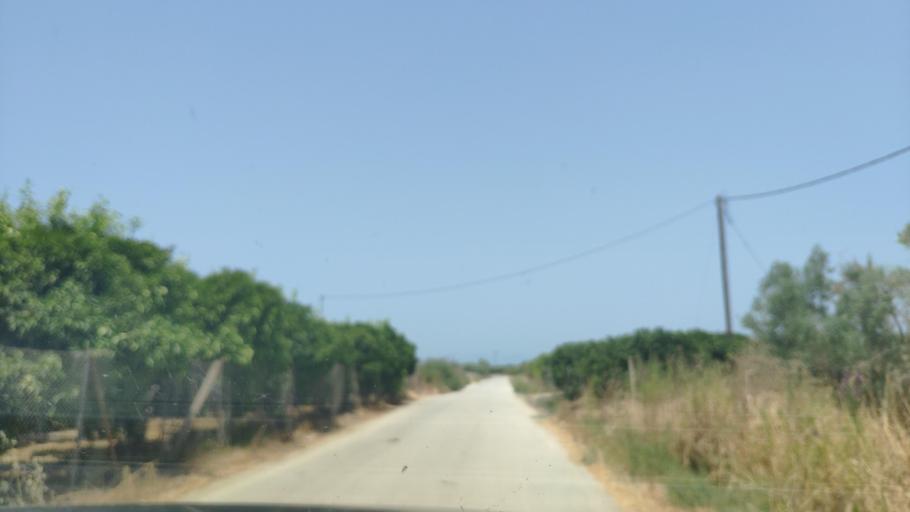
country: GR
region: Epirus
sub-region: Nomos Artas
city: Kompoti
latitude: 39.0596
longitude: 21.0654
